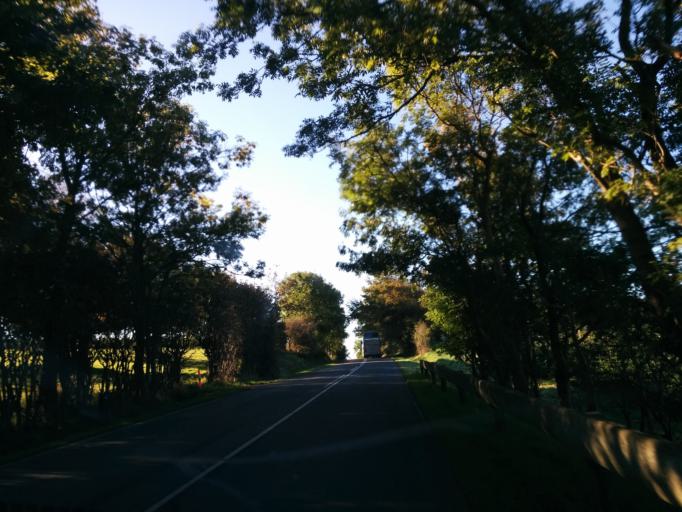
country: DK
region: South Denmark
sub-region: Kolding Kommune
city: Sonder Bjert
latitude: 55.4163
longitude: 9.5613
